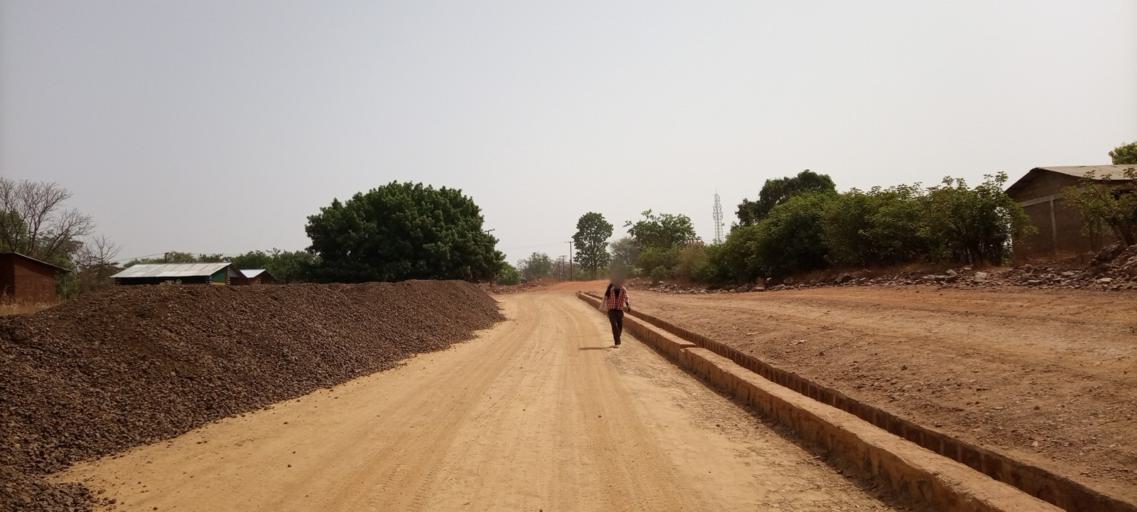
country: ET
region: Oromiya
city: Mendi
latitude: 10.2125
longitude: 35.0830
